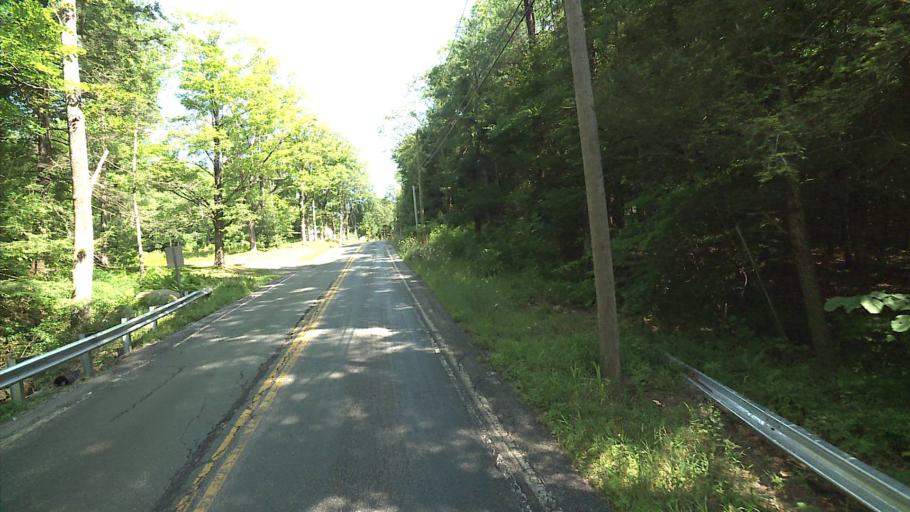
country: US
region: Connecticut
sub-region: Litchfield County
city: Winchester Center
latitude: 41.9371
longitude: -73.2085
